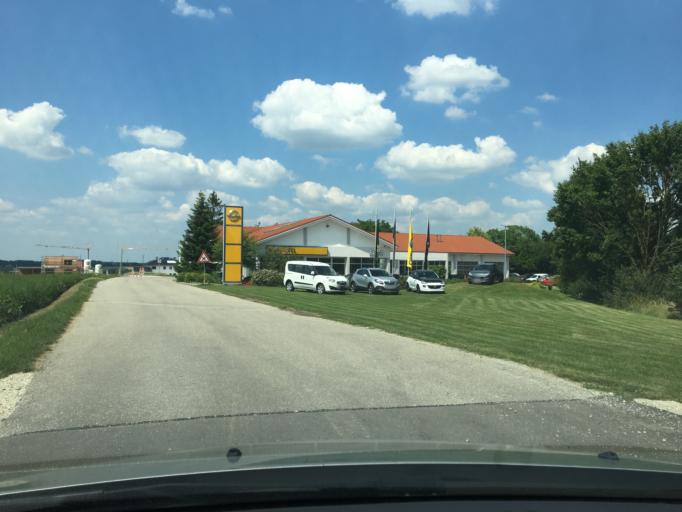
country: DE
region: Bavaria
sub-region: Upper Bavaria
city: Neumarkt-Sankt Veit
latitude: 48.3514
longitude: 12.5090
